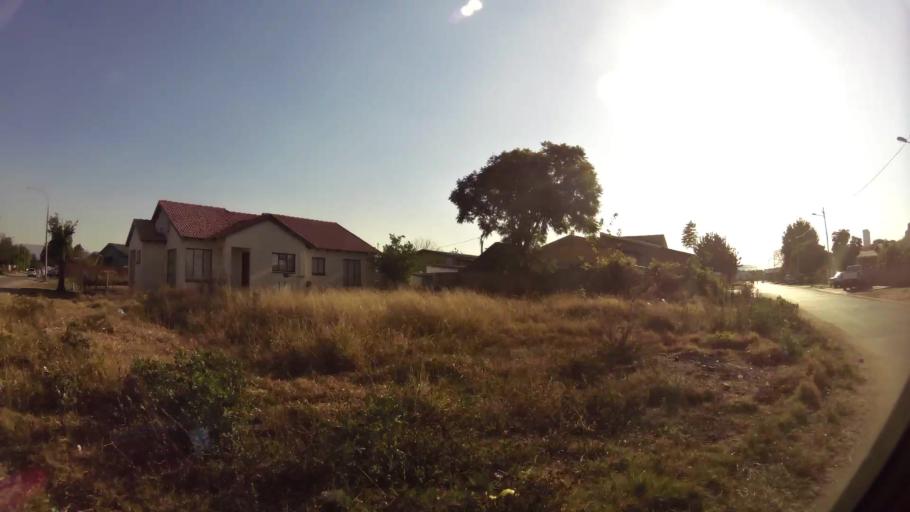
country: ZA
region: North-West
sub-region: Bojanala Platinum District Municipality
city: Rustenburg
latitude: -25.6419
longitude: 27.2393
